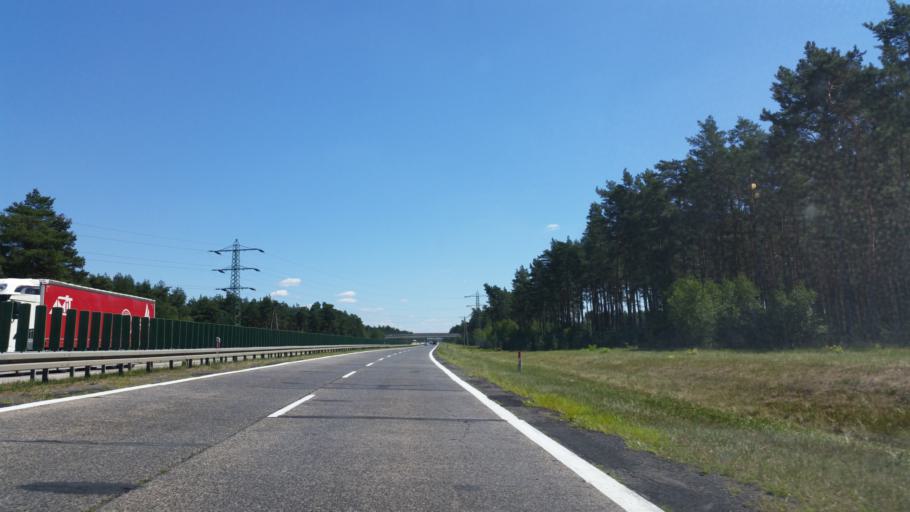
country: PL
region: Lubusz
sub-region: Powiat zaganski
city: Malomice
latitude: 51.4311
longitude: 15.4083
